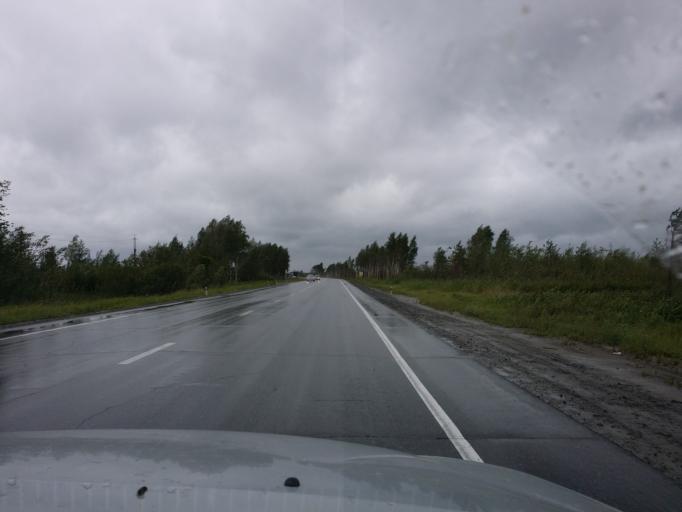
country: RU
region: Khanty-Mansiyskiy Avtonomnyy Okrug
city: Megion
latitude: 61.0674
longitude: 76.2535
